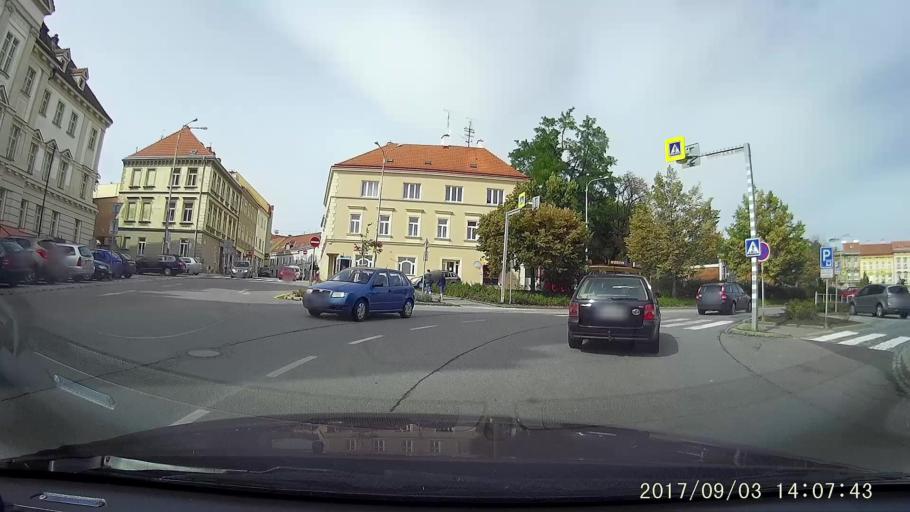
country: CZ
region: South Moravian
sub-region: Okres Znojmo
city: Znojmo
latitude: 48.8525
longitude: 16.0524
